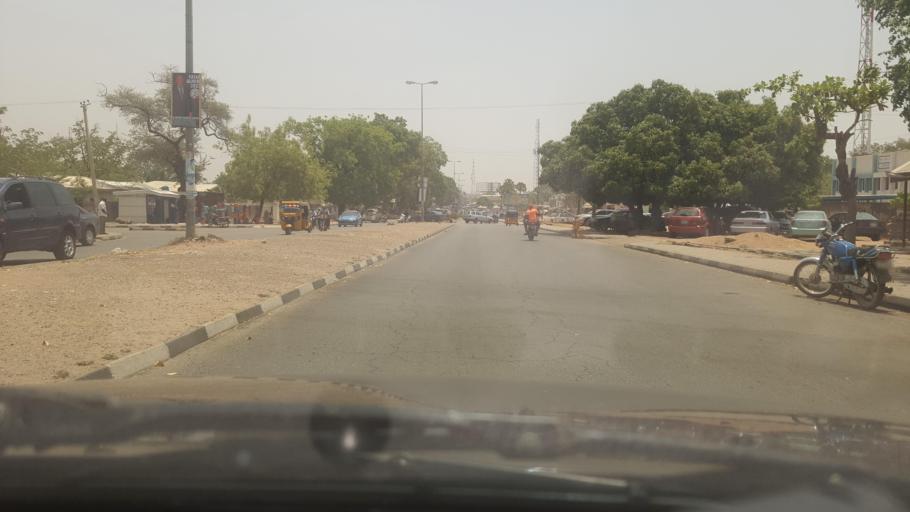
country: NG
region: Bauchi
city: Bauchi
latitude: 10.3166
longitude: 9.8282
